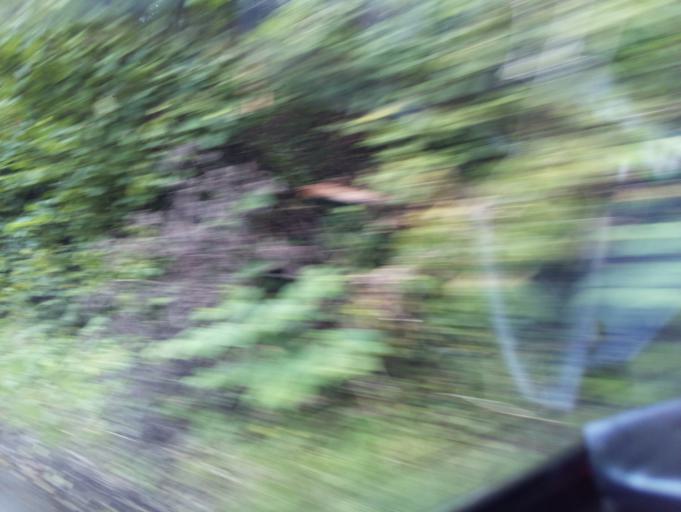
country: GB
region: Wales
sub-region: Cardiff
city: Pentyrch
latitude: 51.5519
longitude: -3.2776
